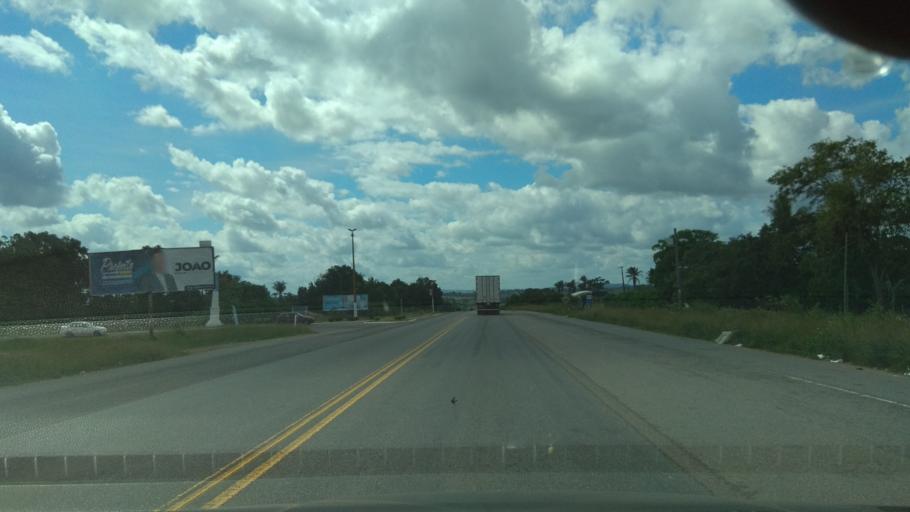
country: BR
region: Bahia
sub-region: Sao Goncalo Dos Campos
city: Sao Goncalo dos Campos
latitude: -12.4303
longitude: -38.9126
